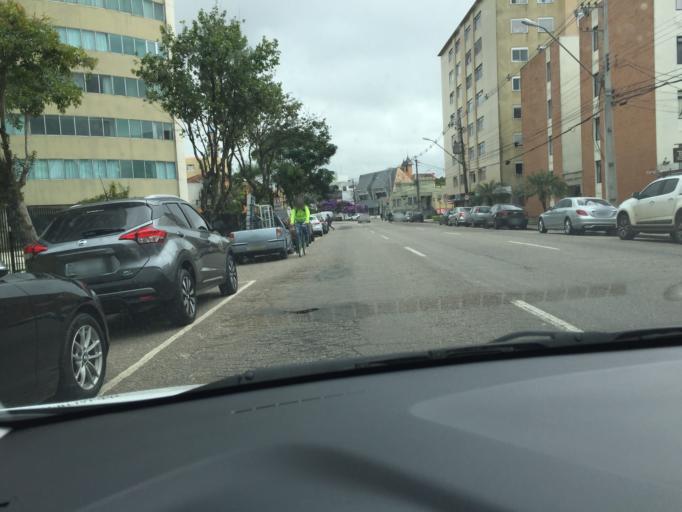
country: BR
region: Parana
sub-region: Curitiba
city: Curitiba
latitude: -25.4223
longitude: -49.2854
